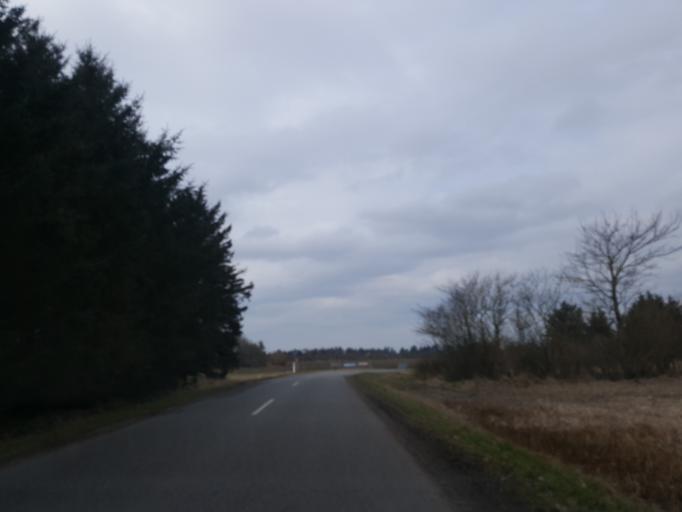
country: DK
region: Central Jutland
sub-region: Holstebro Kommune
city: Ulfborg
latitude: 56.3695
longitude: 8.2306
